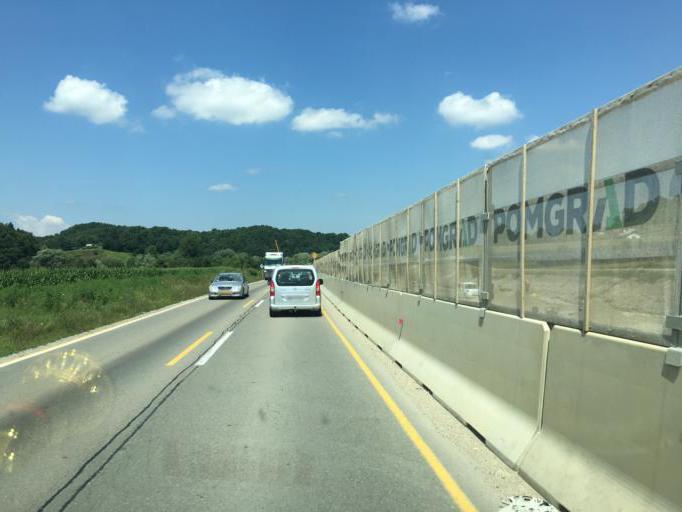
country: SI
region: Podlehnik
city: Podlehnik
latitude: 46.3438
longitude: 15.8724
